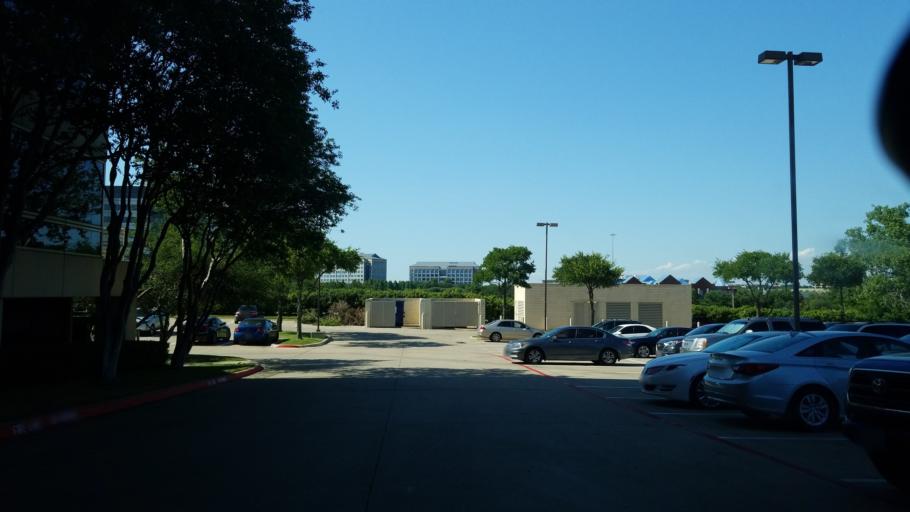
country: US
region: Texas
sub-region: Dallas County
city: Irving
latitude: 32.8879
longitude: -96.9675
